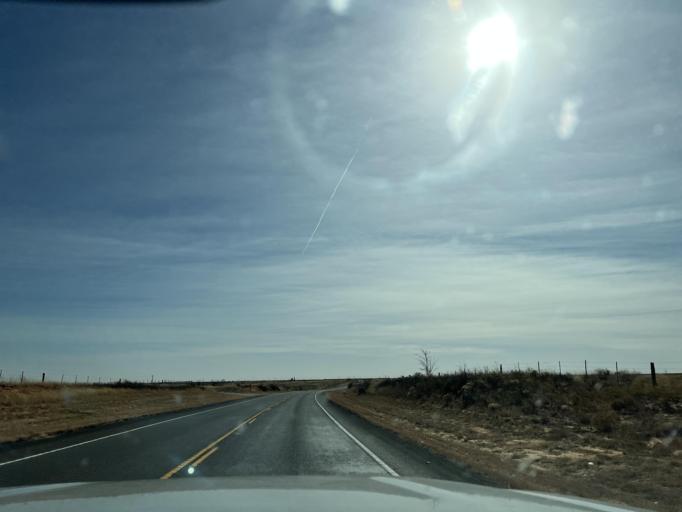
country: US
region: Texas
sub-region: Andrews County
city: Andrews
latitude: 32.4562
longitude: -102.4498
